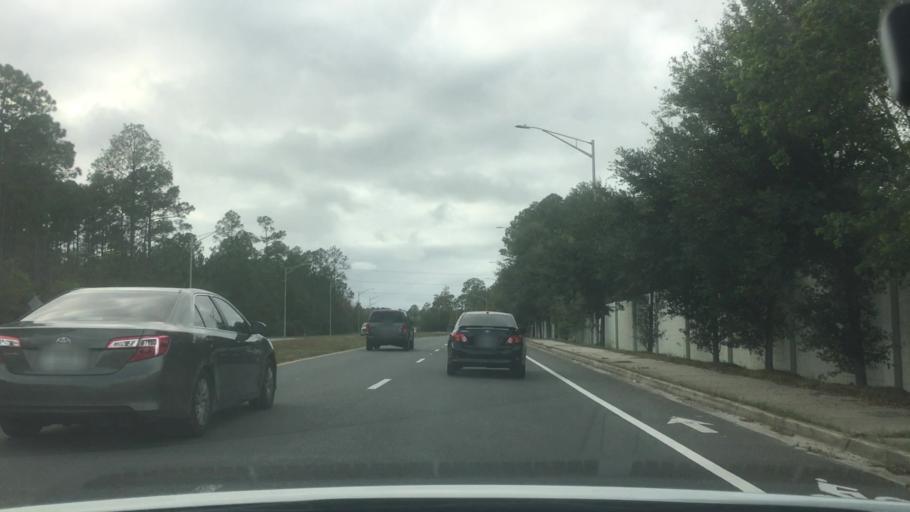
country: US
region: Florida
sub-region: Duval County
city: Jacksonville
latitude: 30.4754
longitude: -81.6106
